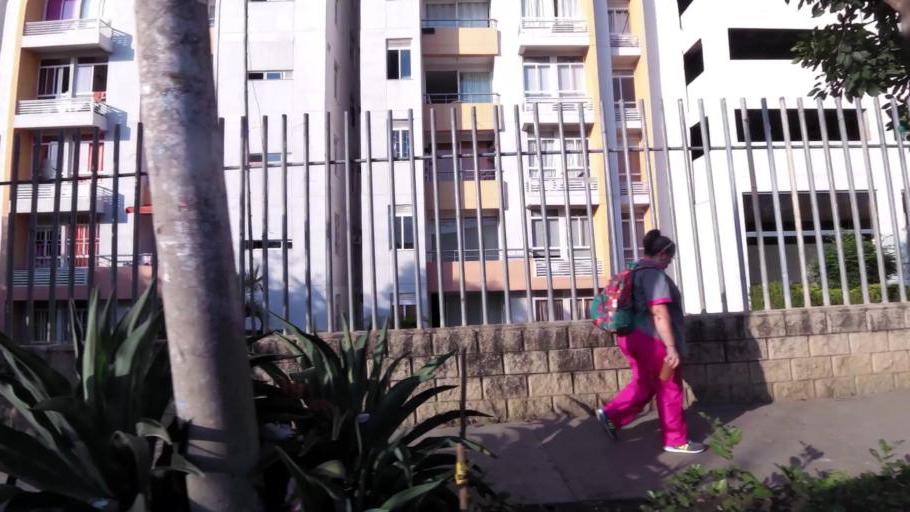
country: CO
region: Bolivar
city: Cartagena
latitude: 10.3879
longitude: -75.4798
